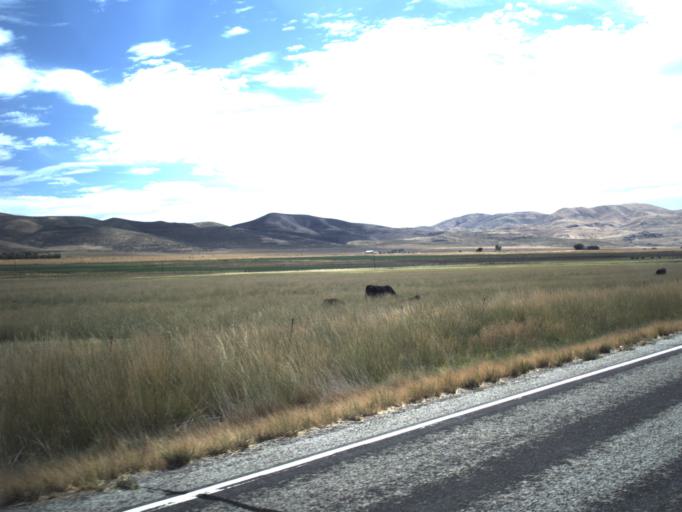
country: US
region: Utah
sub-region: Box Elder County
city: Tremonton
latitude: 41.7614
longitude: -112.4349
